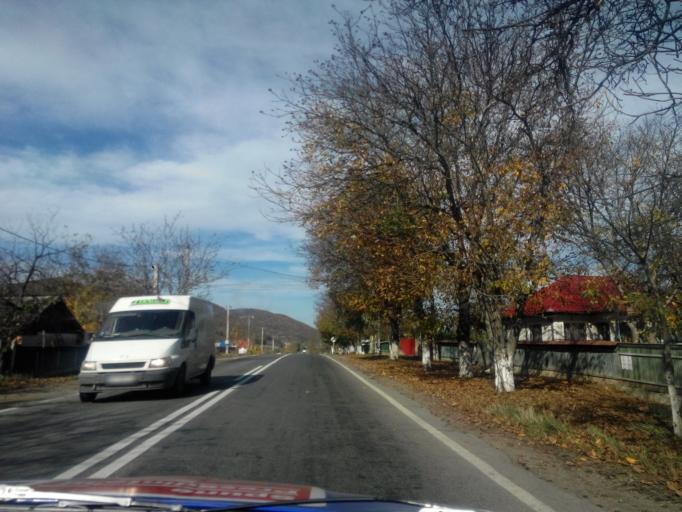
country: RO
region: Bacau
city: Gura Vaii
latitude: 46.3184
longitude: 26.7487
